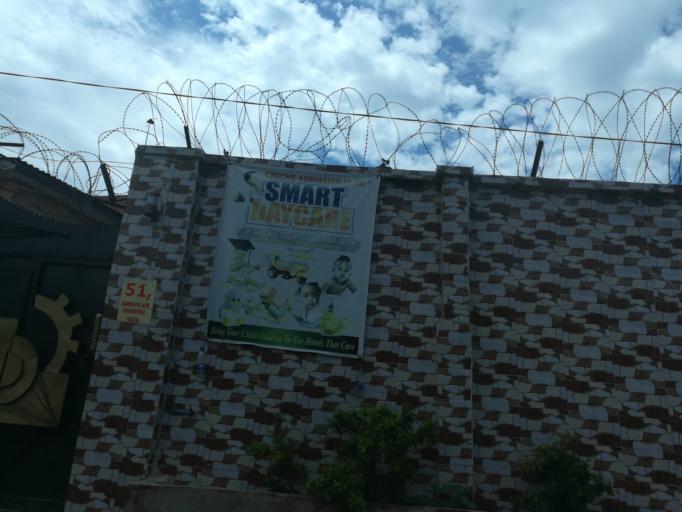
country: NG
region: Lagos
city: Agege
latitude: 6.6058
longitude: 3.3244
